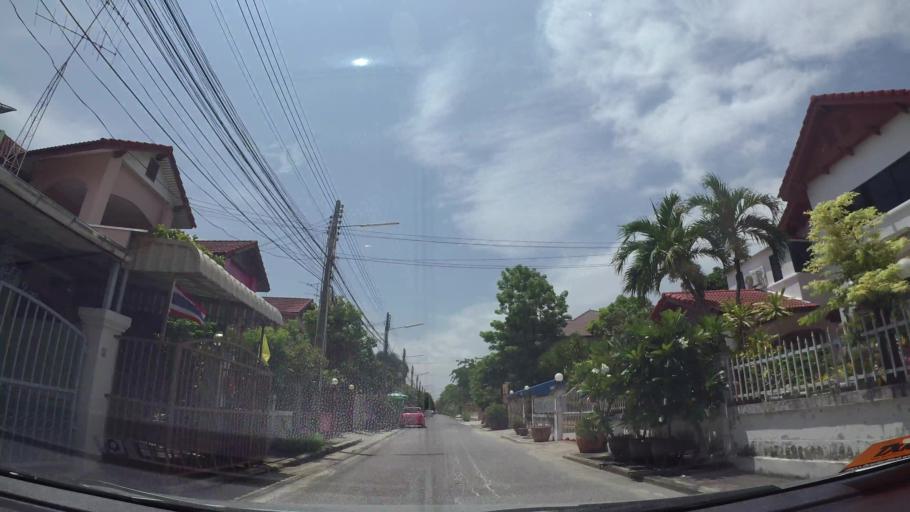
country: TH
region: Chon Buri
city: Chon Buri
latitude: 13.3333
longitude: 100.9379
